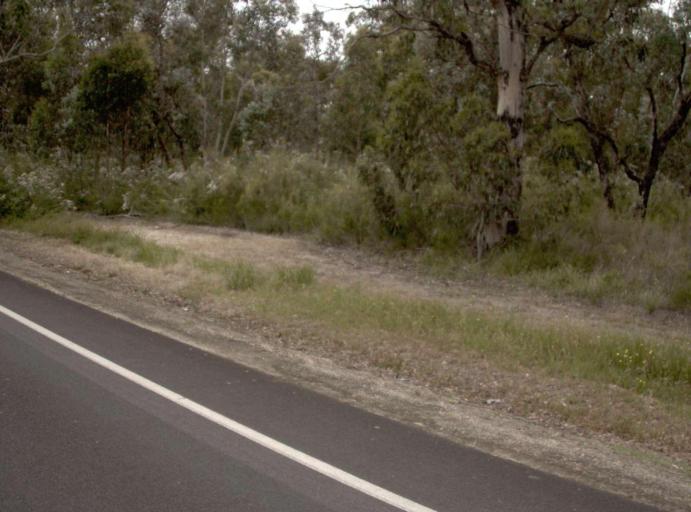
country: AU
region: Victoria
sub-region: Wellington
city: Sale
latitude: -38.3197
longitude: 147.0228
